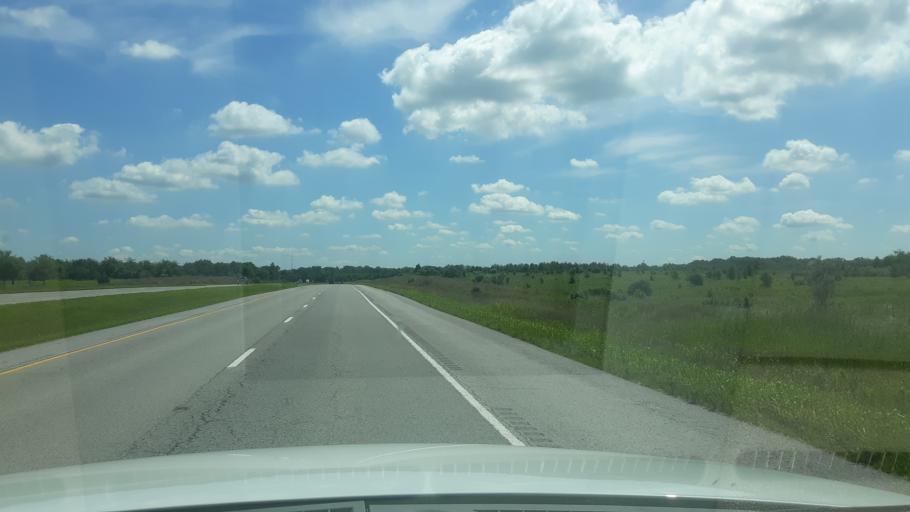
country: US
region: Illinois
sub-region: Saline County
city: Harrisburg
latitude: 37.7307
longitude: -88.5856
